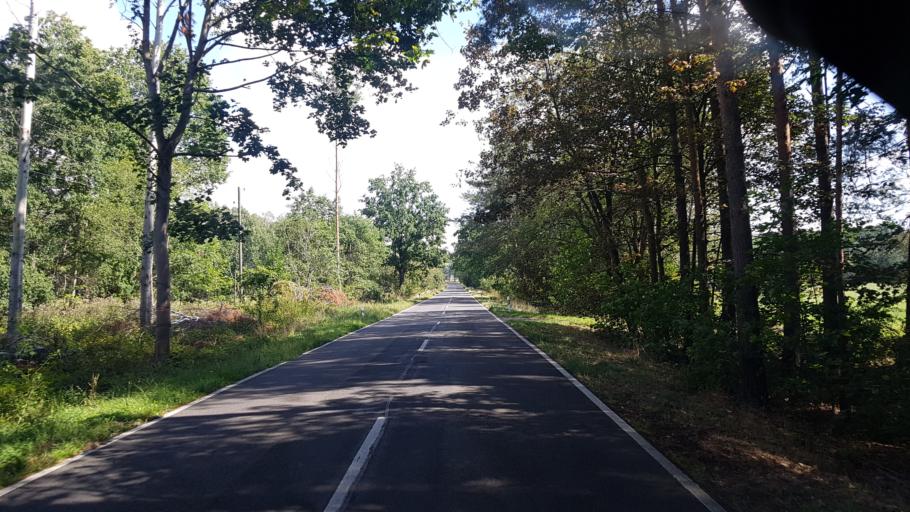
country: DE
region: Brandenburg
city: Drebkau
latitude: 51.6532
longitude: 14.3089
